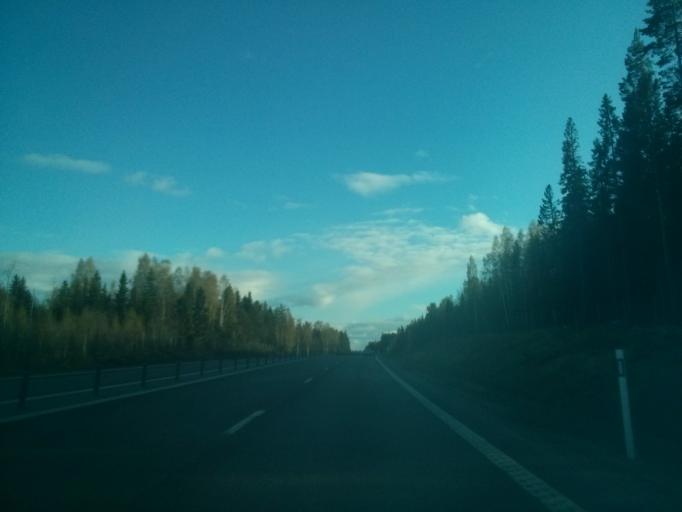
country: SE
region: Vaesternorrland
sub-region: Sundsvalls Kommun
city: Njurundabommen
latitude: 62.1285
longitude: 17.3355
